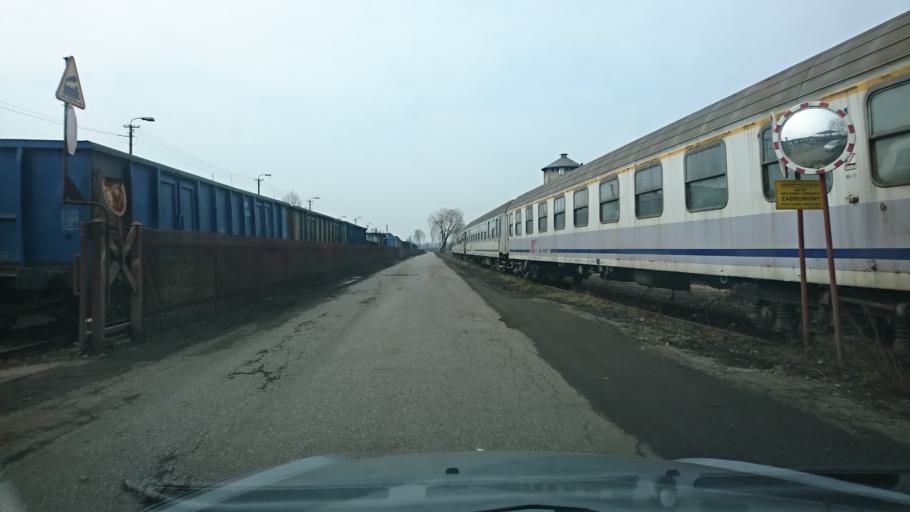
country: PL
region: Lesser Poland Voivodeship
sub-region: Powiat wielicki
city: Czarnochowice
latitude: 50.0243
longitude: 20.0241
